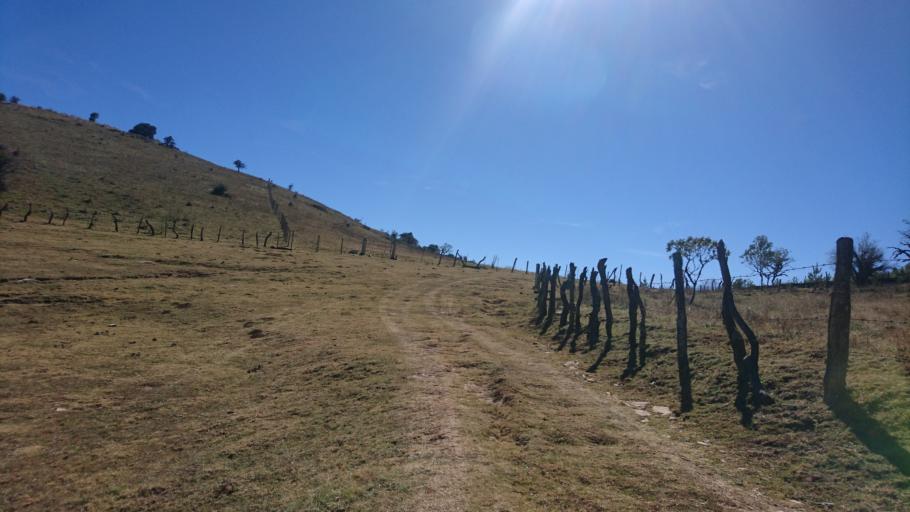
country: MX
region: San Luis Potosi
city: Zaragoza
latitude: 22.0195
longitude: -100.6212
